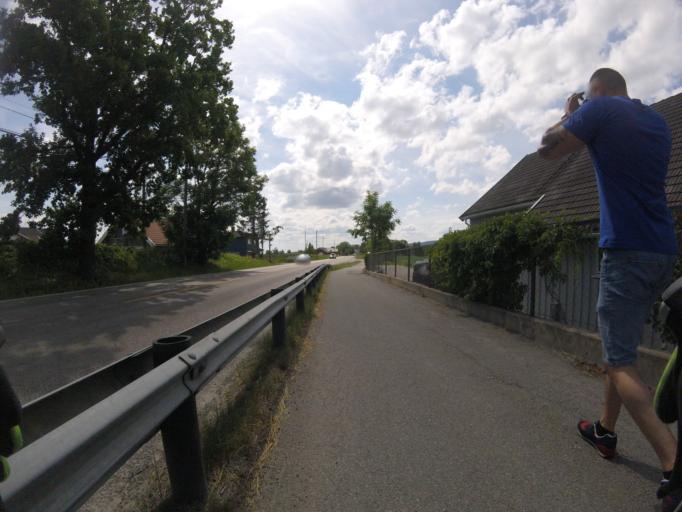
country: NO
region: Akershus
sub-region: Skedsmo
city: Lillestrom
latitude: 59.9768
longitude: 11.0570
